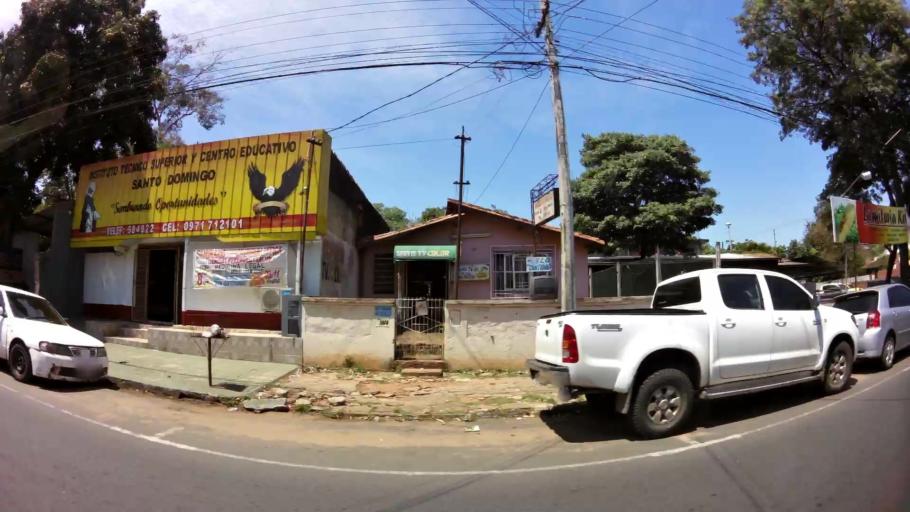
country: PY
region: Central
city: San Lorenzo
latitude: -25.3484
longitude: -57.5083
